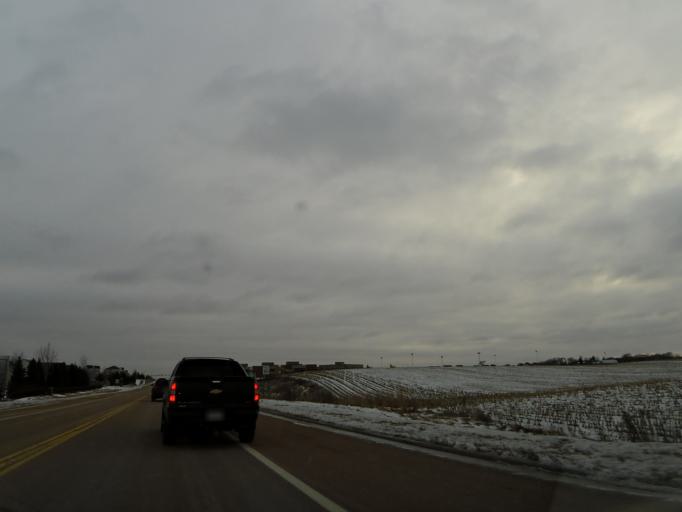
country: US
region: Minnesota
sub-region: Carver County
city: Carver
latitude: 44.7748
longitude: -93.6428
